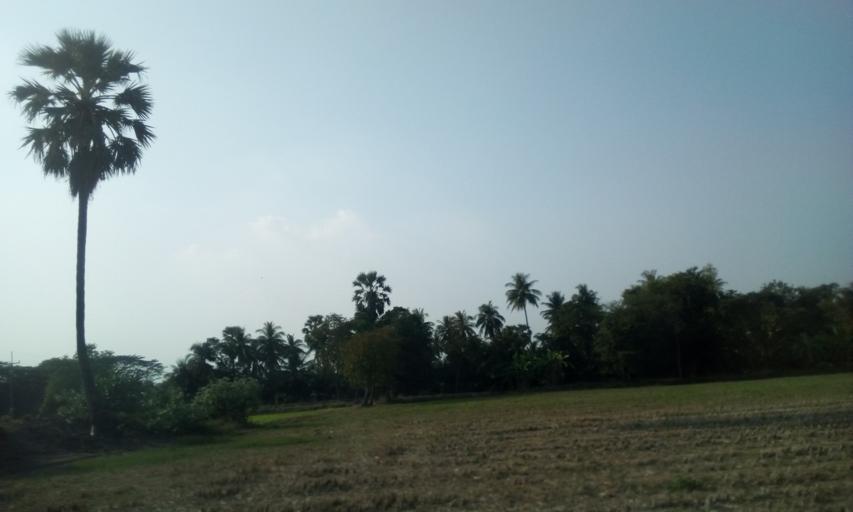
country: TH
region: Sing Buri
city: Sing Buri
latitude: 14.8338
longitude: 100.3999
